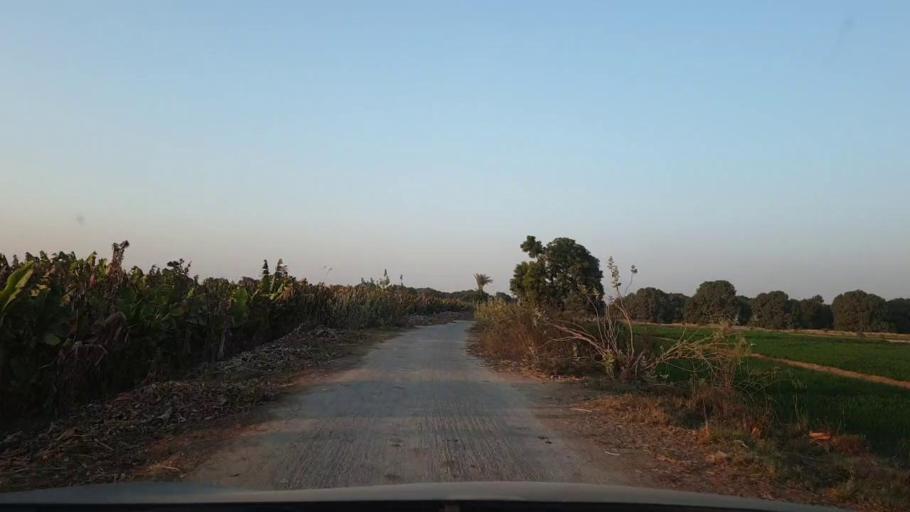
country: PK
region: Sindh
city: Tando Allahyar
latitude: 25.5266
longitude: 68.7354
